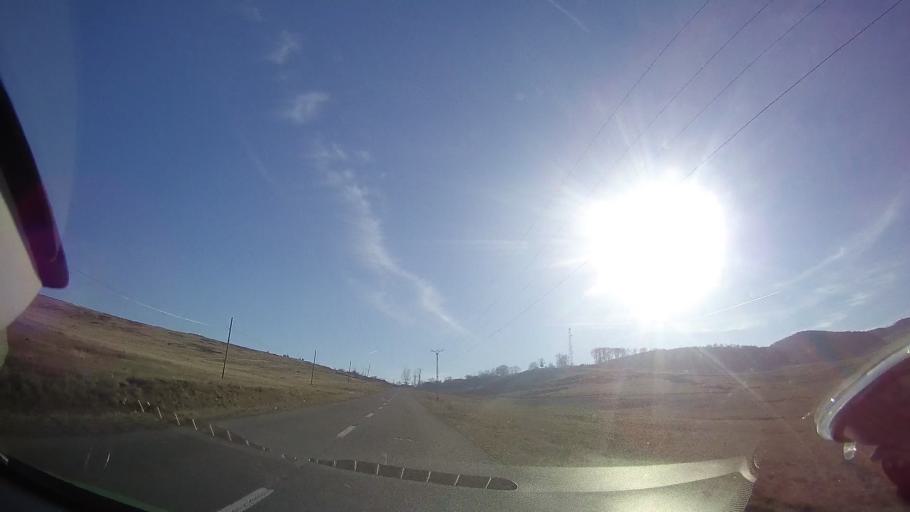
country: RO
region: Bihor
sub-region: Comuna Vadu Crisului
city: Vadu Crisului
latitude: 46.9800
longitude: 22.5322
